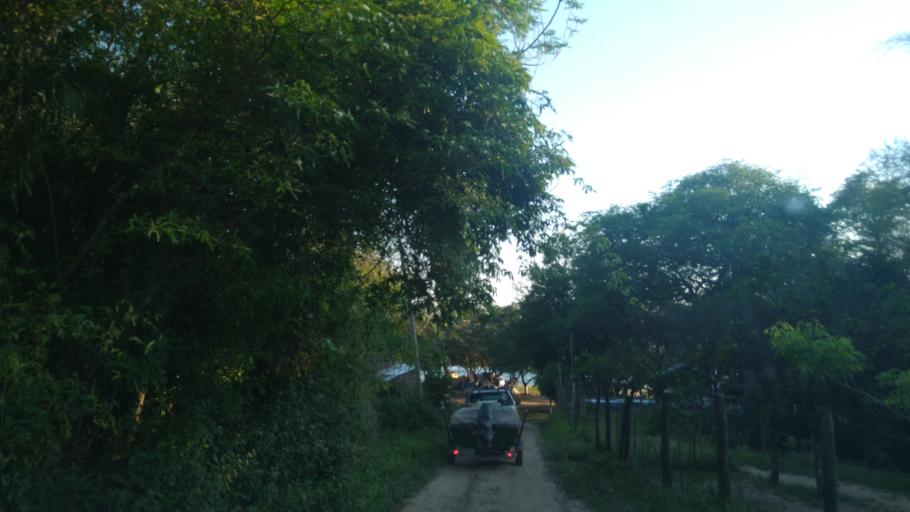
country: PY
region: Neembucu
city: Cerrito
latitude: -27.3698
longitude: -57.6566
